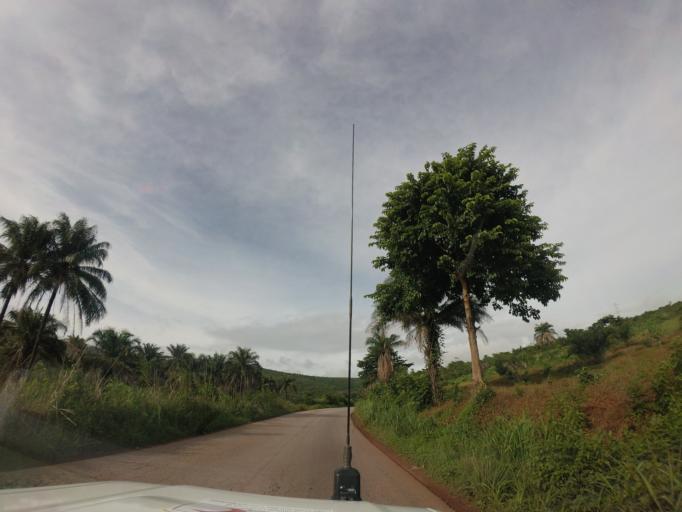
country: GN
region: Kindia
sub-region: Kindia
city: Kindia
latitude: 9.9078
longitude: -12.9959
